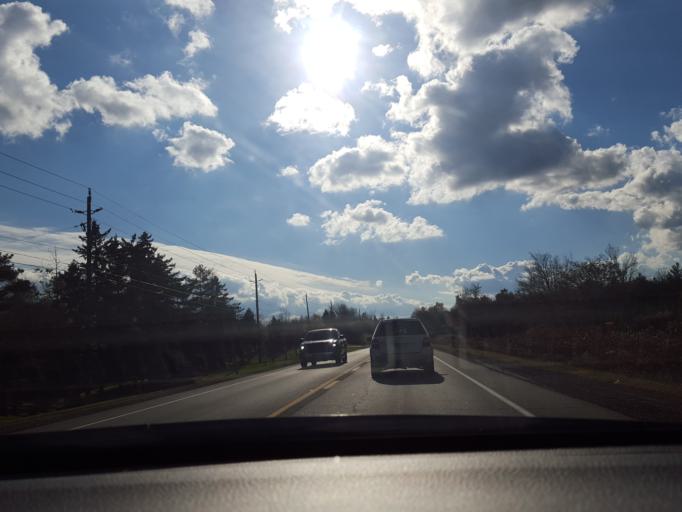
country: CA
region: Ontario
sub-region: Halton
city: Milton
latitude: 43.4648
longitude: -79.9078
